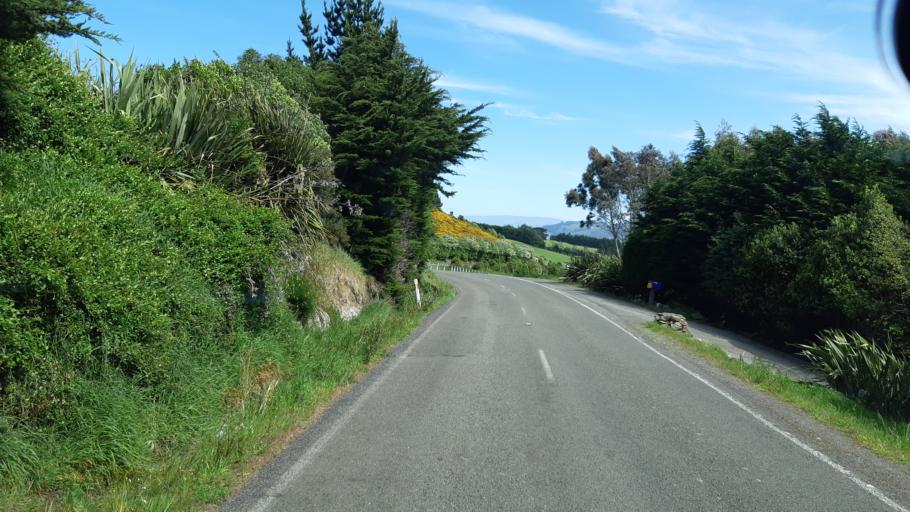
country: NZ
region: Otago
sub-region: Dunedin City
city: Dunedin
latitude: -45.8855
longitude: 170.5694
